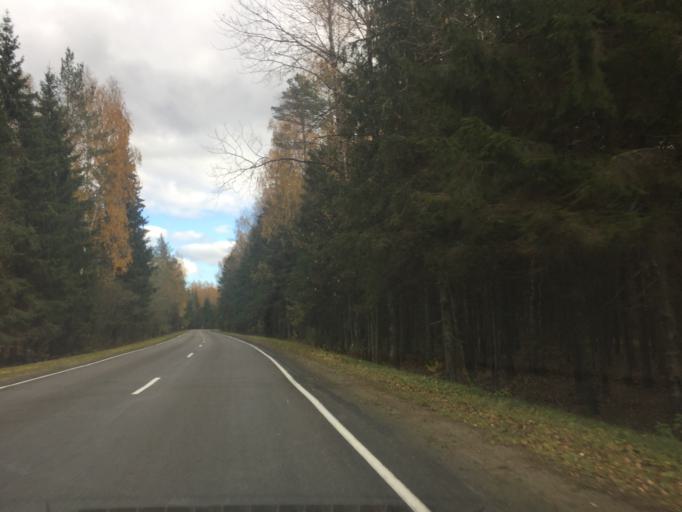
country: BY
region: Minsk
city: Svir
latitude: 54.9253
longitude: 26.4893
